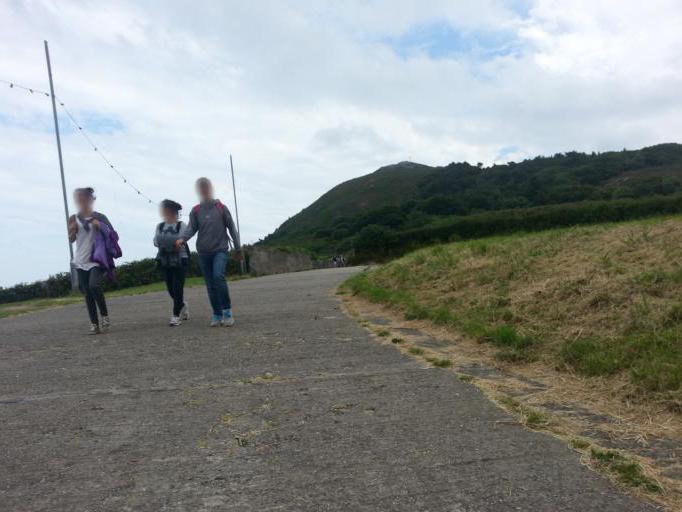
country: IE
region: Leinster
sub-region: Wicklow
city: Bray
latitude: 53.1961
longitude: -6.0893
